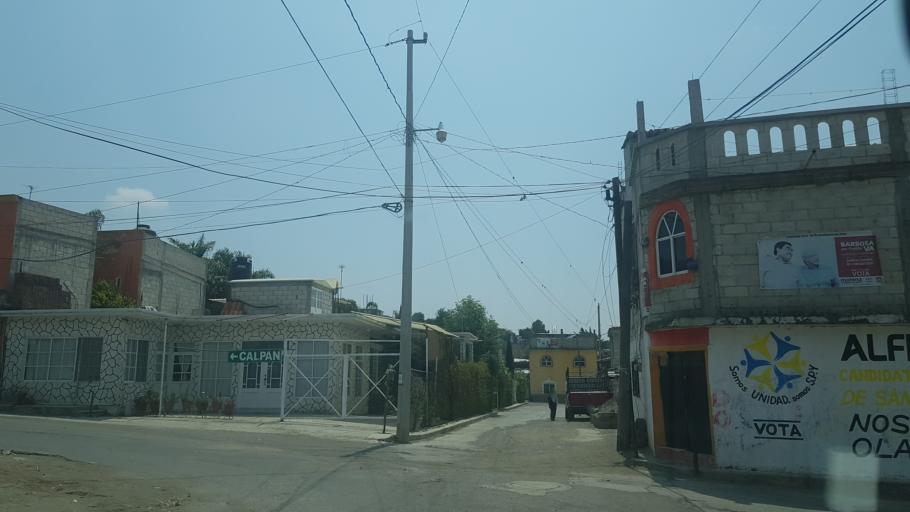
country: MX
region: Puebla
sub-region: San Nicolas de los Ranchos
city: San Pedro Yancuitlalpan
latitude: 19.0775
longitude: -98.4820
